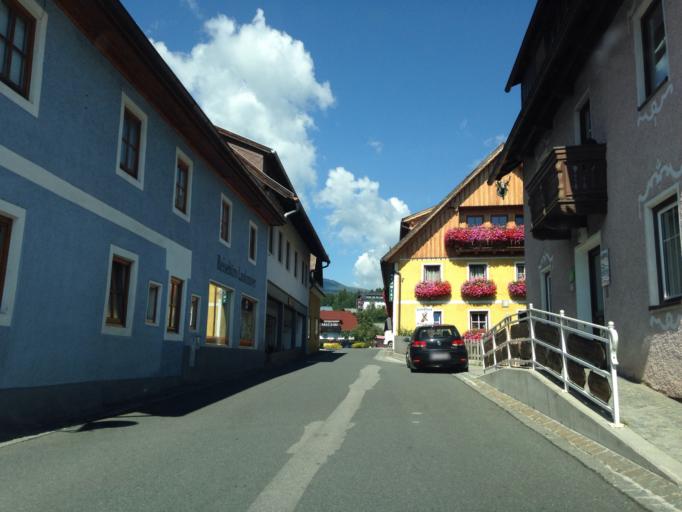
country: AT
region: Salzburg
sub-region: Politischer Bezirk Tamsweg
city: Mariapfarr
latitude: 47.1503
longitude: 13.7434
